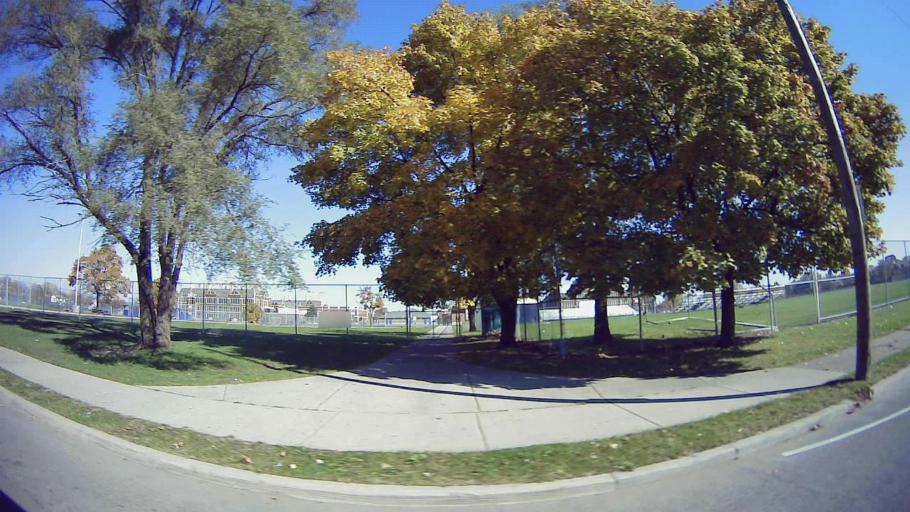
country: US
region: Michigan
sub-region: Wayne County
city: Highland Park
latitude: 42.3823
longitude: -83.1146
